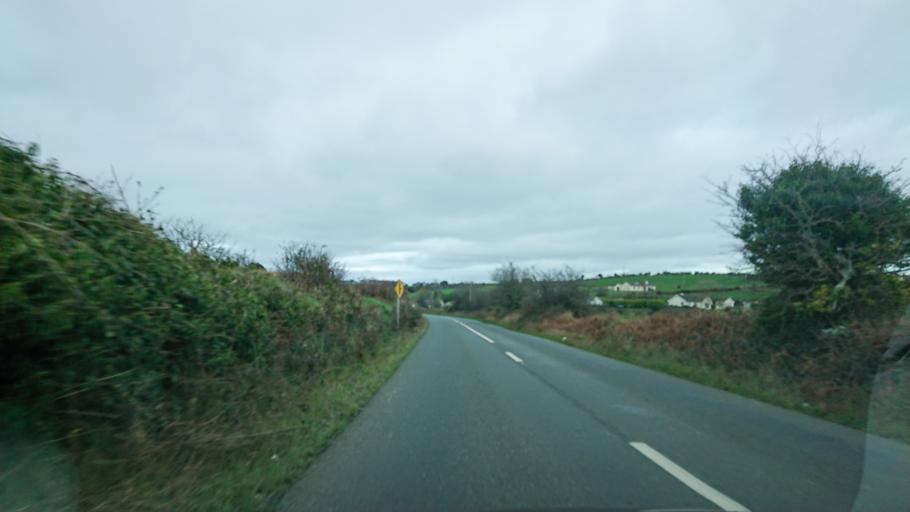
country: IE
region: Leinster
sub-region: Kilkenny
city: Mooncoin
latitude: 52.2162
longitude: -7.2401
